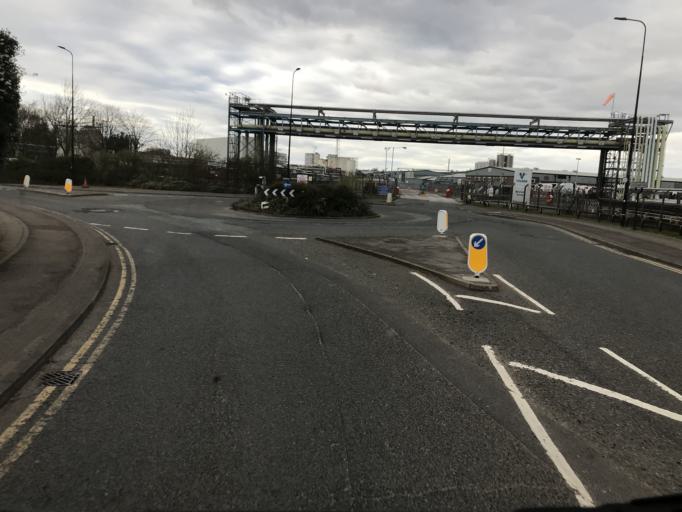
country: GB
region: England
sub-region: Trafford
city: Trafford Park
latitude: 53.4730
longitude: -2.3104
